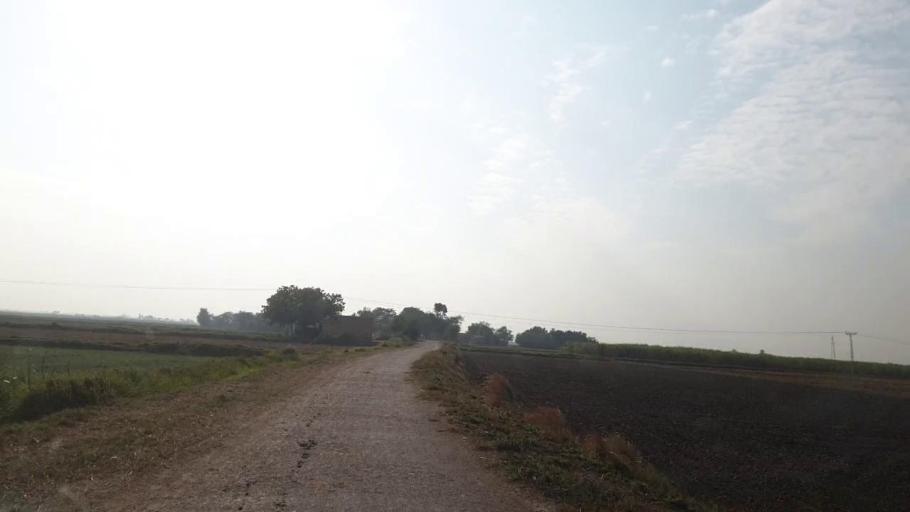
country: PK
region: Sindh
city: Chuhar Jamali
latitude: 24.3859
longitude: 68.0079
